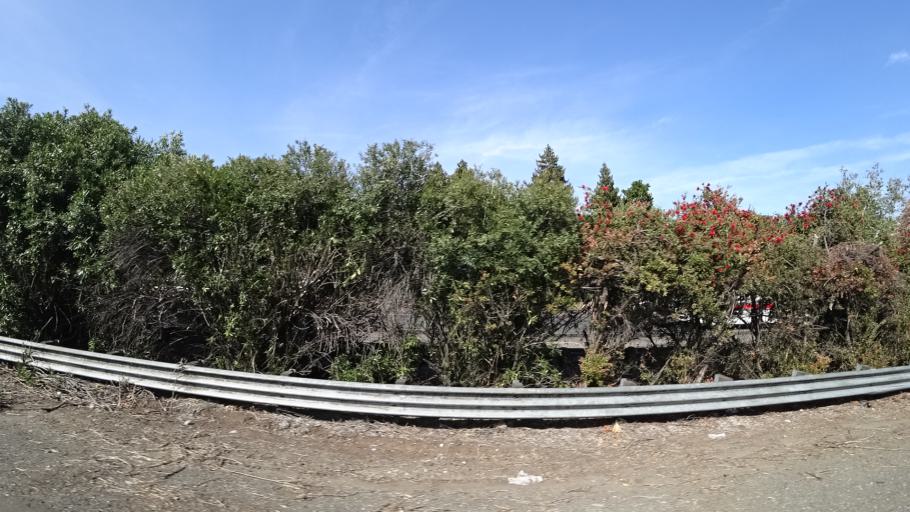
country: US
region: California
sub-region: Butte County
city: Chico
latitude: 39.7531
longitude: -121.8434
